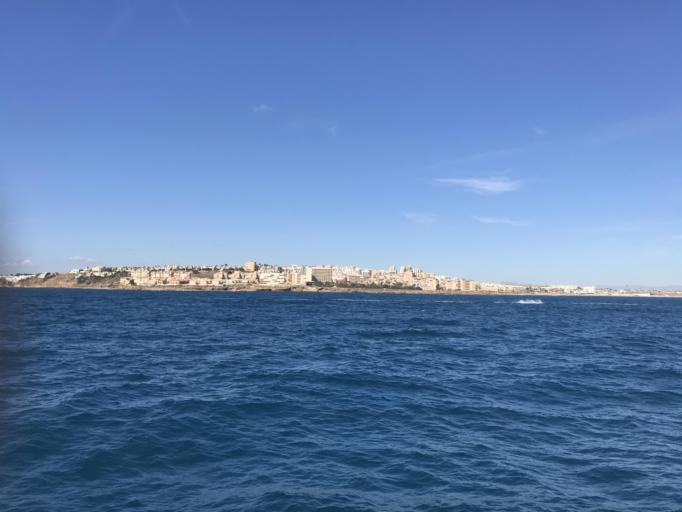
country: ES
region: Valencia
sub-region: Provincia de Alicante
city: Torrevieja
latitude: 38.0006
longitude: -0.6373
